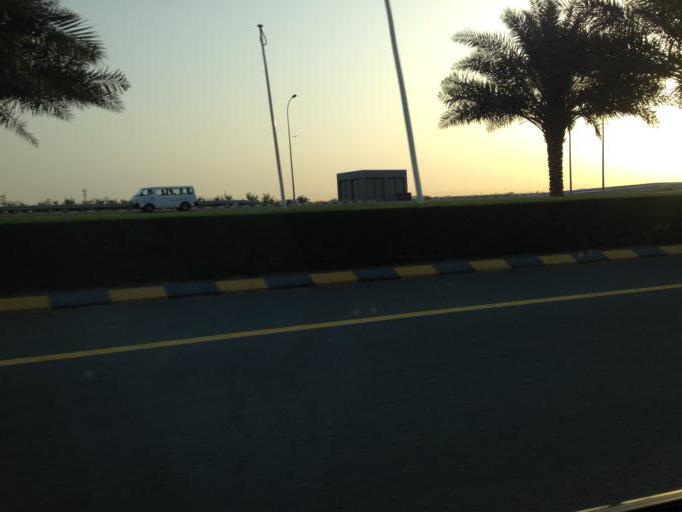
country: OM
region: Muhafazat Masqat
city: Bawshar
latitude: 23.5999
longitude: 58.3276
